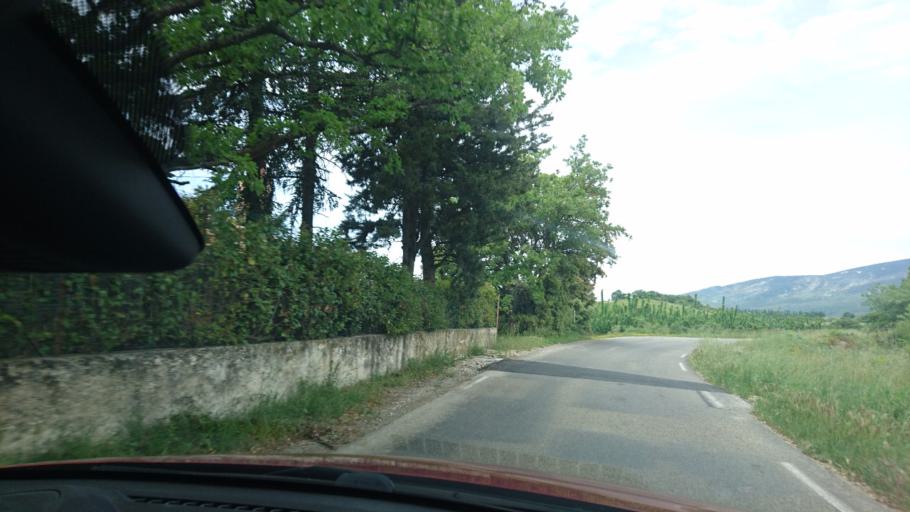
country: FR
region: Provence-Alpes-Cote d'Azur
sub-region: Departement du Vaucluse
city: Villes-sur-Auzon
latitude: 44.0859
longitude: 5.2360
